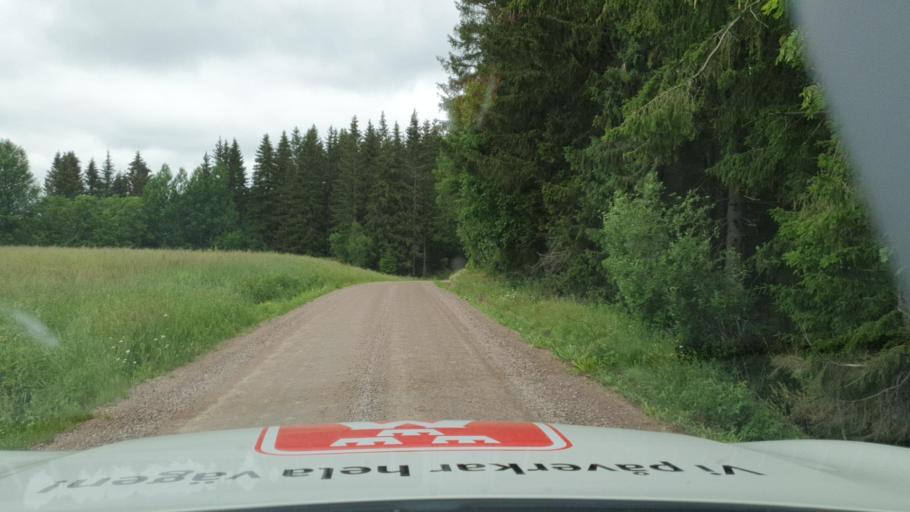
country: SE
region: Vaermland
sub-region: Filipstads Kommun
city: Filipstad
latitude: 59.5534
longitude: 13.9795
